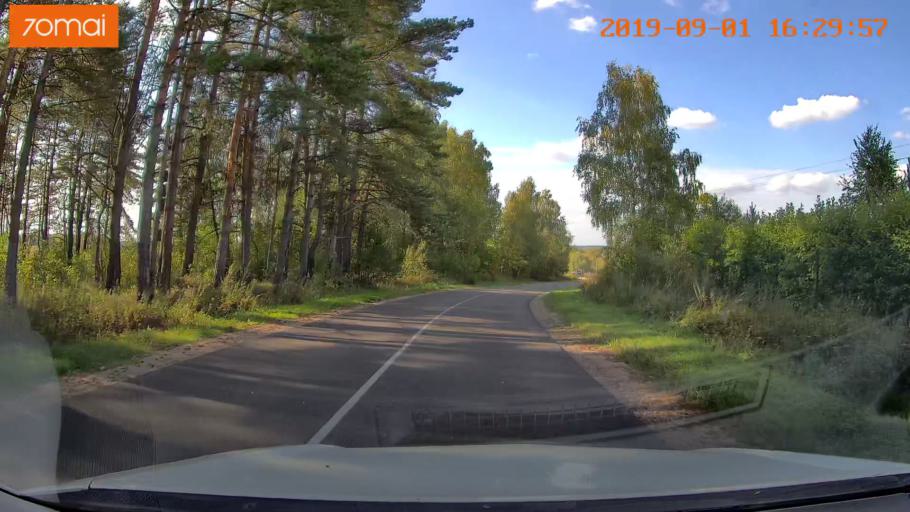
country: RU
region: Kaluga
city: Maloyaroslavets
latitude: 54.9401
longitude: 36.4602
